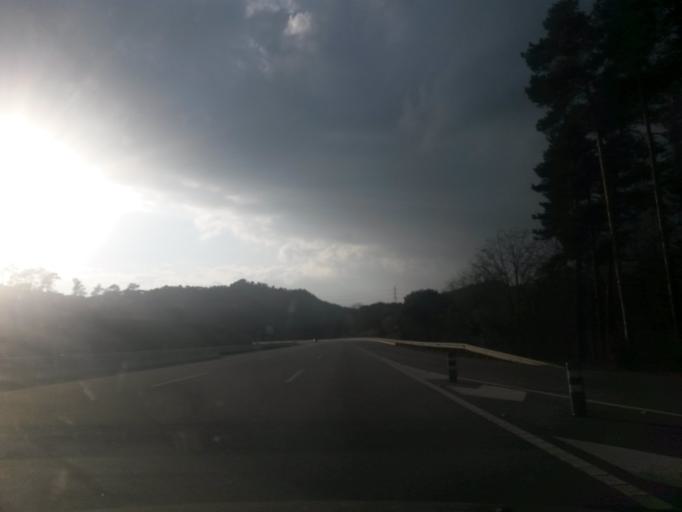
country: ES
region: Catalonia
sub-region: Provincia de Barcelona
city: Sant Julia de Vilatorta
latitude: 41.8922
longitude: 2.3549
